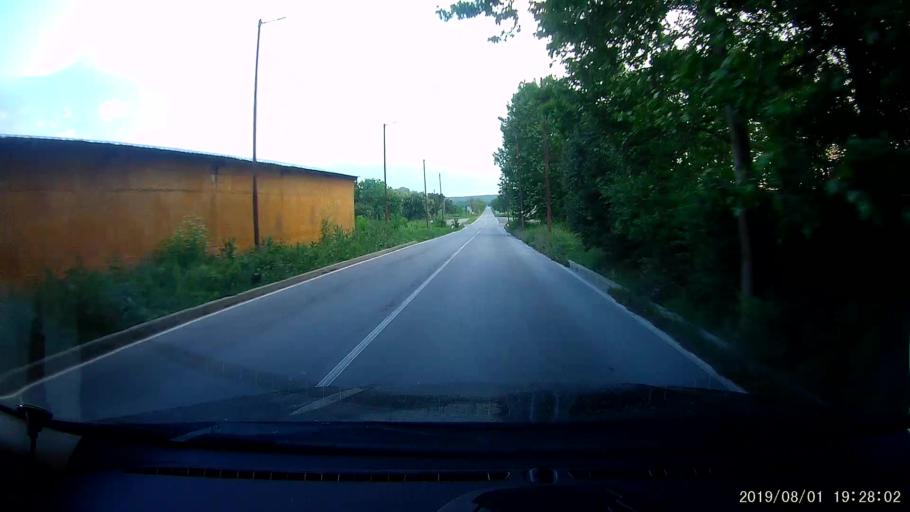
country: BG
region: Burgas
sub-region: Obshtina Sungurlare
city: Sungurlare
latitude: 42.8472
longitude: 26.9248
